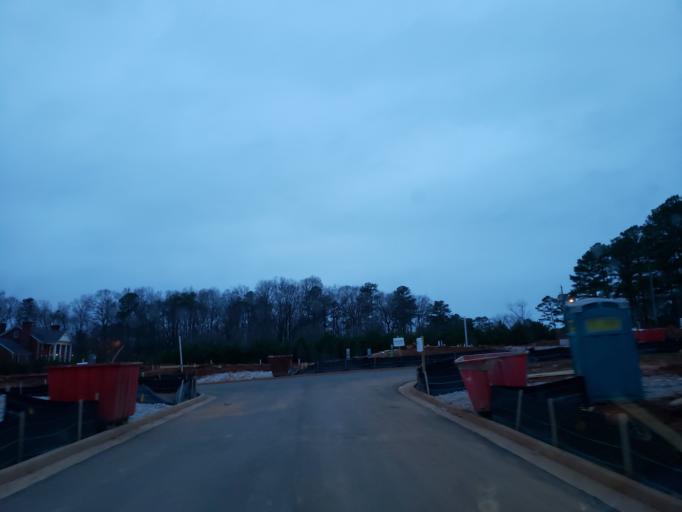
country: US
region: Georgia
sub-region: Cobb County
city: Mableton
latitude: 33.8397
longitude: -84.5824
